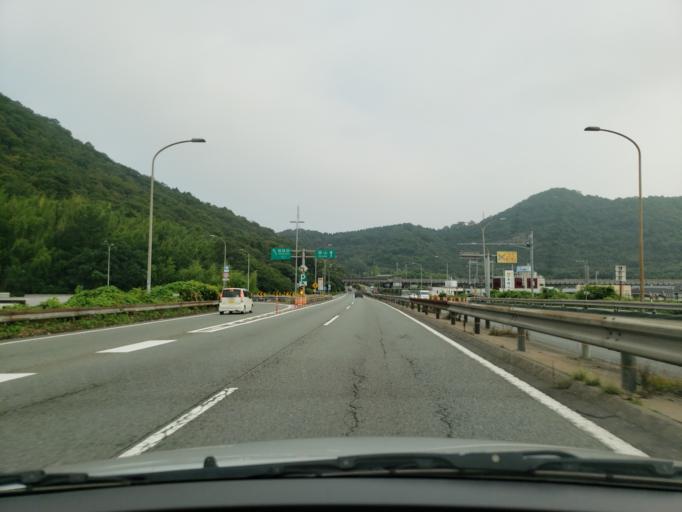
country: JP
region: Hyogo
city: Himeji
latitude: 34.8287
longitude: 134.6336
